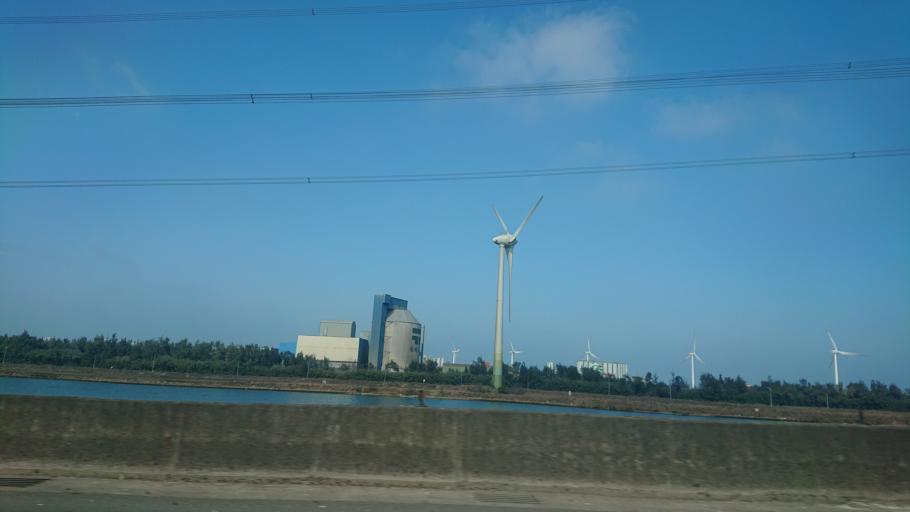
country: TW
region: Taiwan
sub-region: Changhua
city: Chang-hua
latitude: 24.1499
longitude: 120.4531
